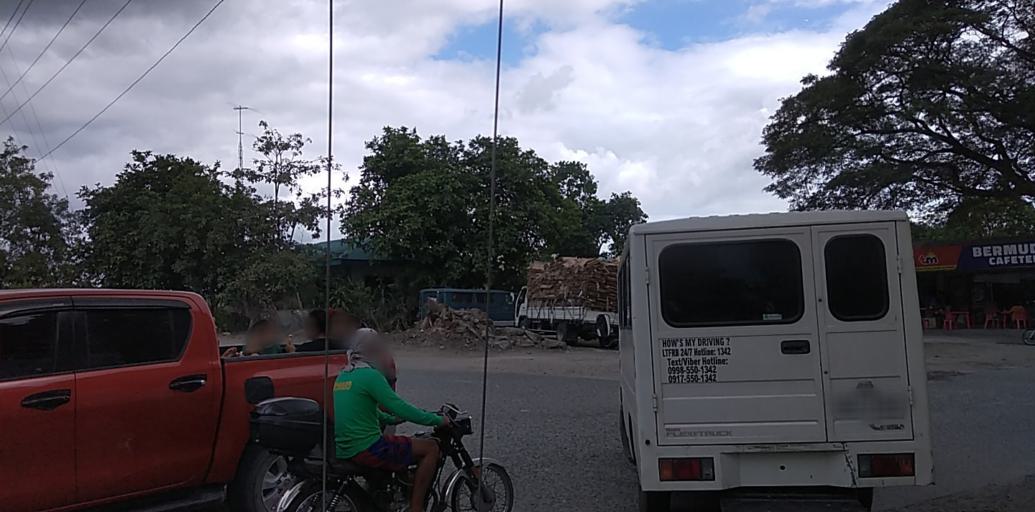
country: PH
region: Central Luzon
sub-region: Province of Pampanga
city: Porac
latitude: 15.0652
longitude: 120.5482
